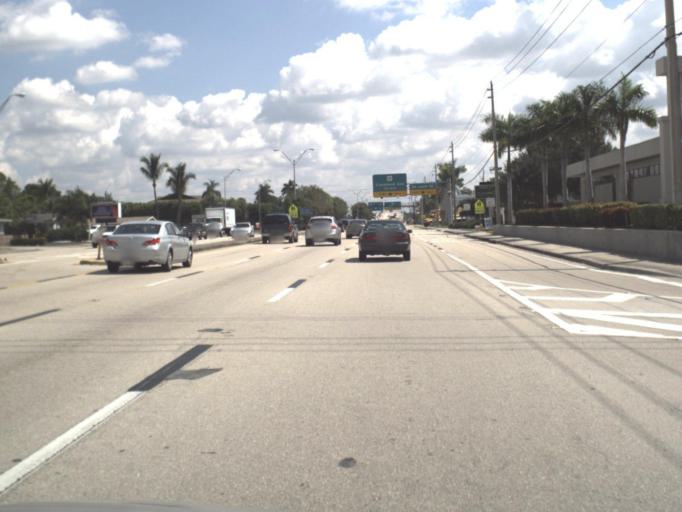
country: US
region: Florida
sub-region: Lee County
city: Pine Manor
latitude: 26.5967
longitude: -81.8799
